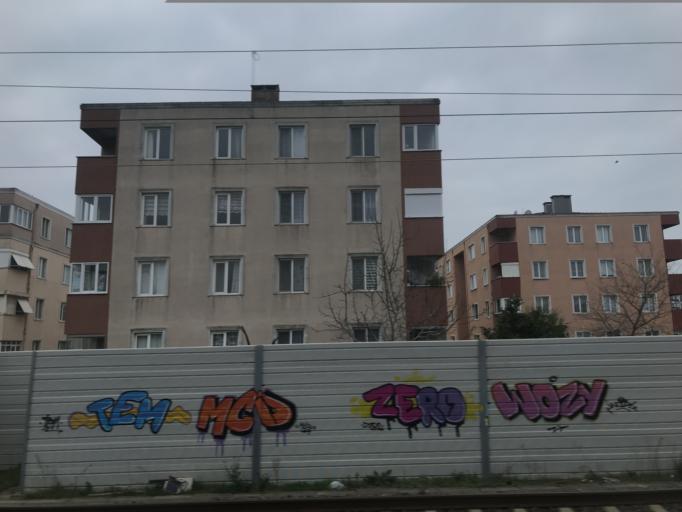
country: TR
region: Istanbul
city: Icmeler
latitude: 40.8421
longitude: 29.3048
